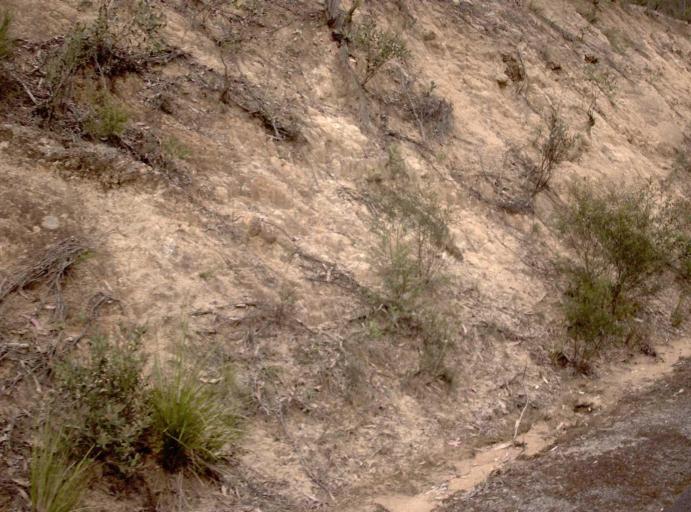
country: AU
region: New South Wales
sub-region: Bombala
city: Bombala
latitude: -37.3521
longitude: 149.2026
